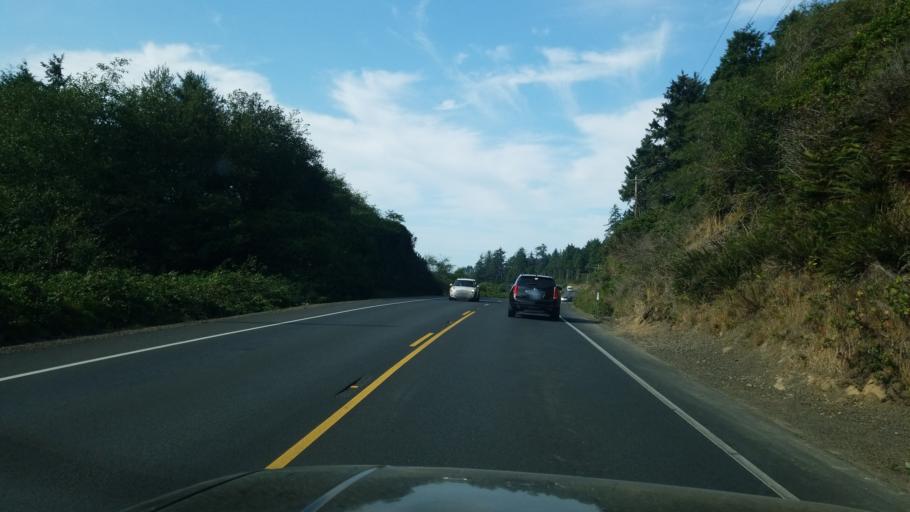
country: US
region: Oregon
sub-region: Tillamook County
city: Rockaway Beach
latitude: 45.5774
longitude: -123.9452
